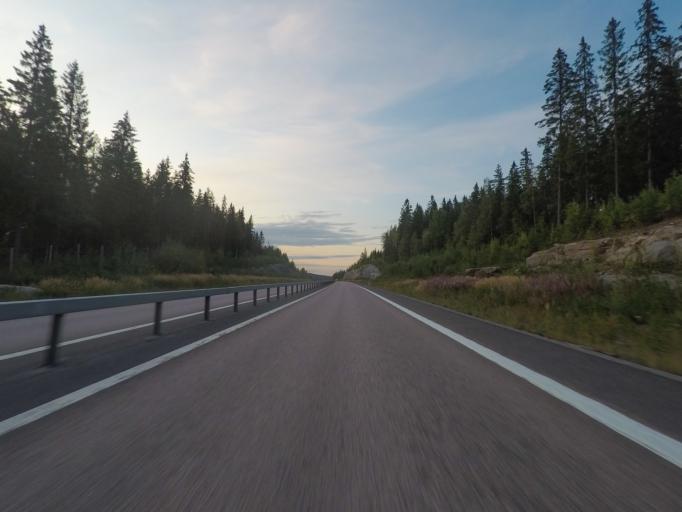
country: FI
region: Central Finland
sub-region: Jyvaeskylae
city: Saeynaetsalo
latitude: 62.1794
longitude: 25.9066
